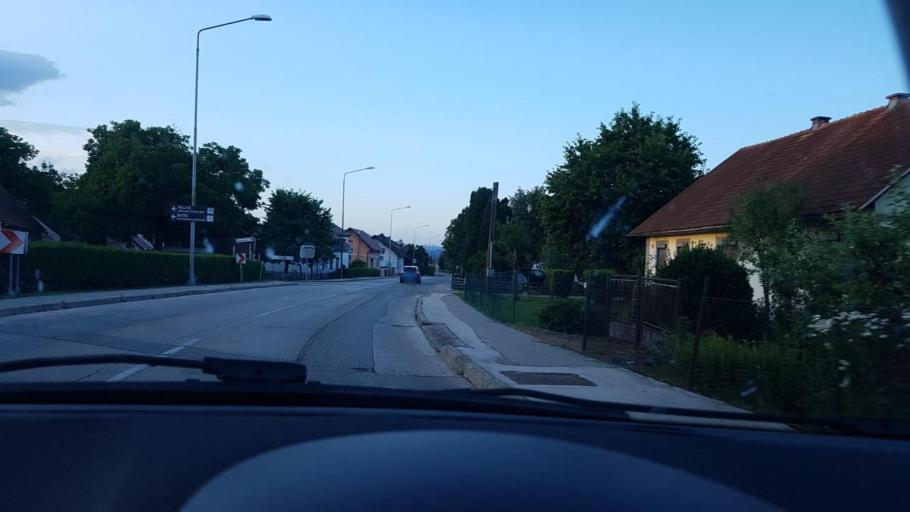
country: SI
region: Brezice
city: Brezice
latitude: 45.9151
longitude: 15.5905
